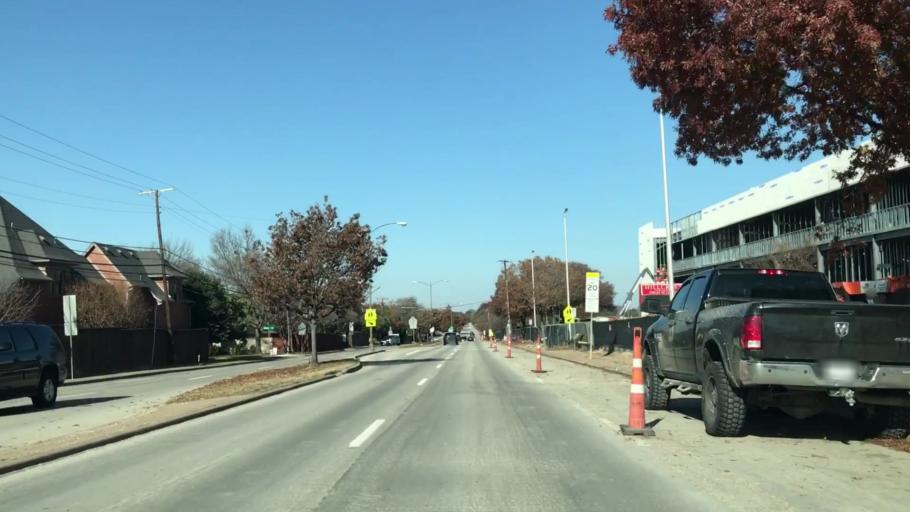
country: US
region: Texas
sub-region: Dallas County
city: University Park
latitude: 32.8825
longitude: -96.7866
